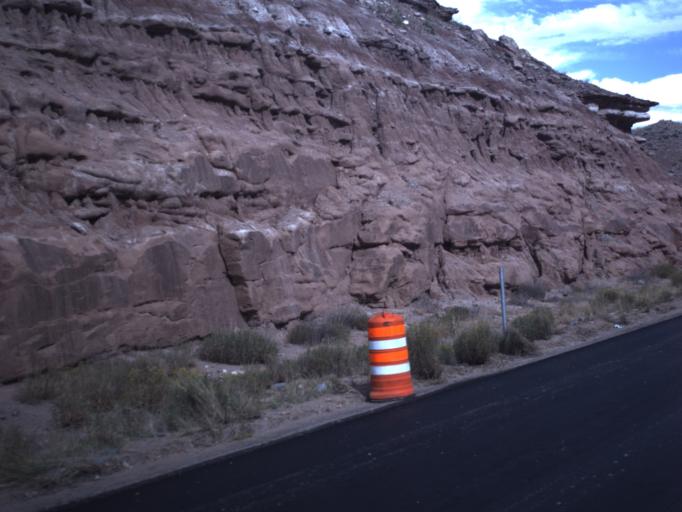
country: US
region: Colorado
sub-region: Montezuma County
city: Towaoc
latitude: 37.2248
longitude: -109.2069
